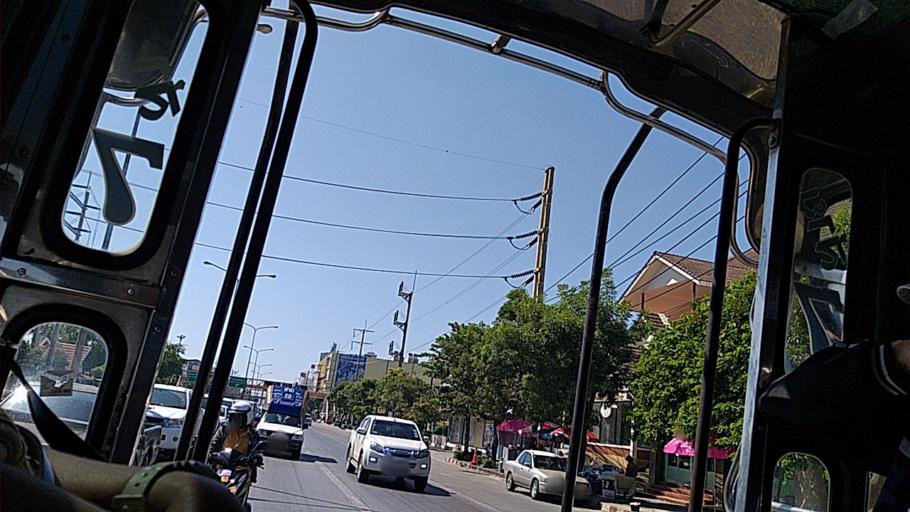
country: TH
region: Nakhon Ratchasima
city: Nakhon Ratchasima
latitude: 14.9801
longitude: 102.1004
